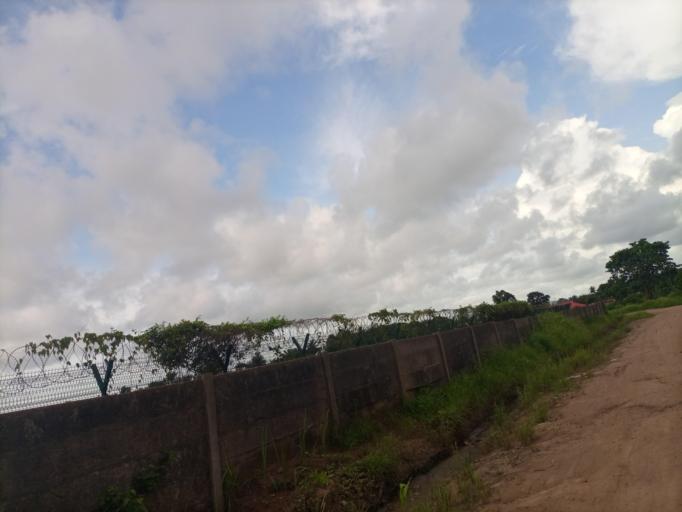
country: SL
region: Northern Province
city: Masoyila
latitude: 8.6105
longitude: -13.1783
